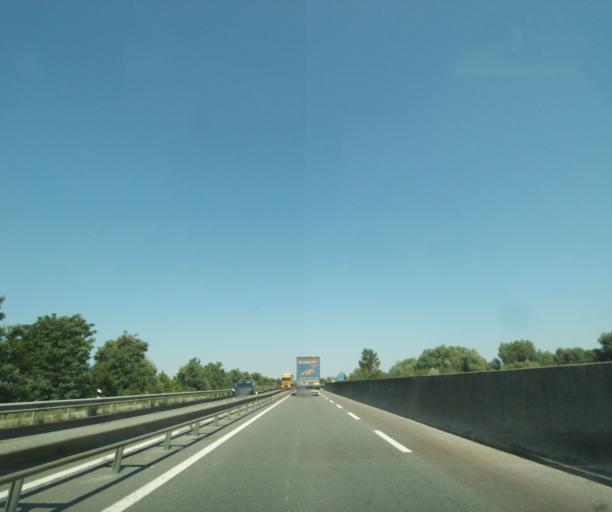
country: FR
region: Champagne-Ardenne
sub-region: Departement de la Haute-Marne
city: Saint-Dizier
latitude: 48.6288
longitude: 4.9302
